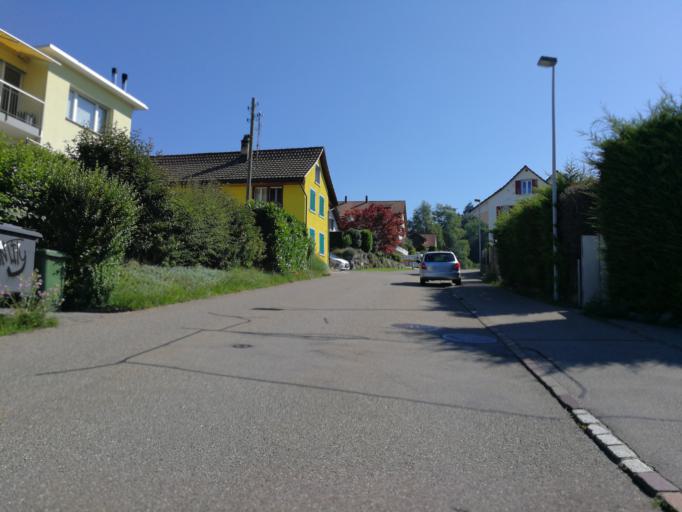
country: CH
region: Zurich
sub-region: Bezirk Hinwil
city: Hadlikon
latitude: 47.2887
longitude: 8.8585
